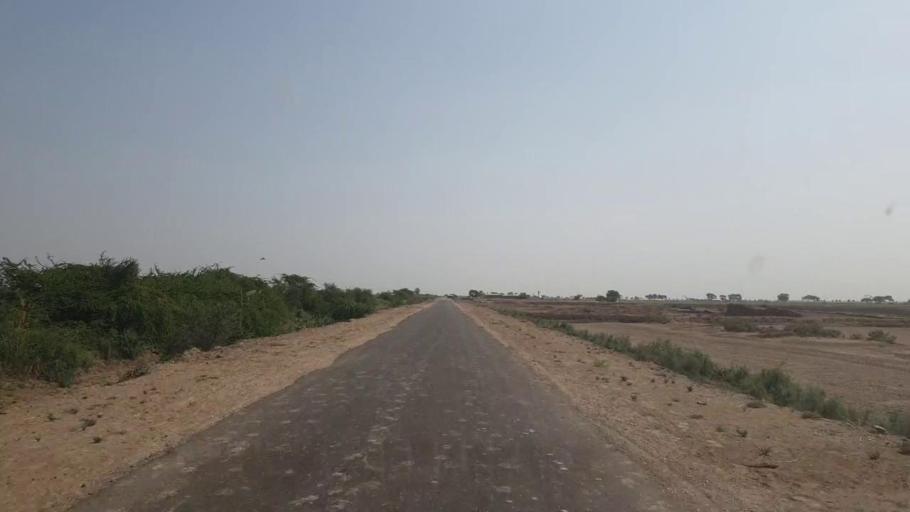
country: PK
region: Sindh
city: Jati
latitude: 24.4629
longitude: 68.5111
